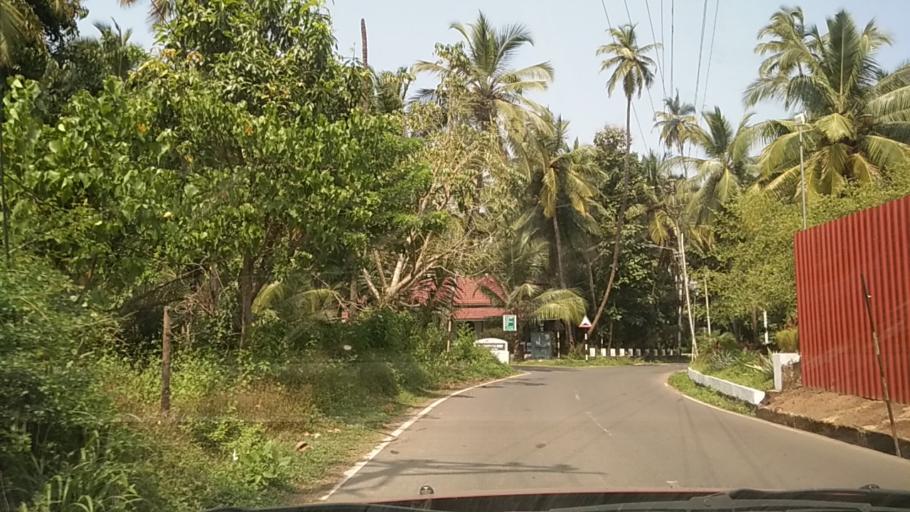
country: IN
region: Goa
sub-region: South Goa
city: Sancoale
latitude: 15.3394
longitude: 73.8999
